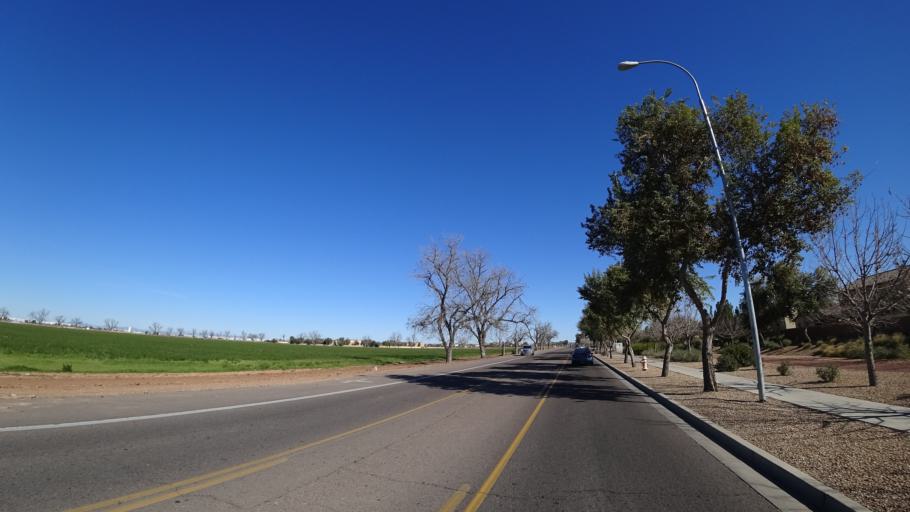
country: US
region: Arizona
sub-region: Maricopa County
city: Tolleson
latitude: 33.4211
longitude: -112.2630
